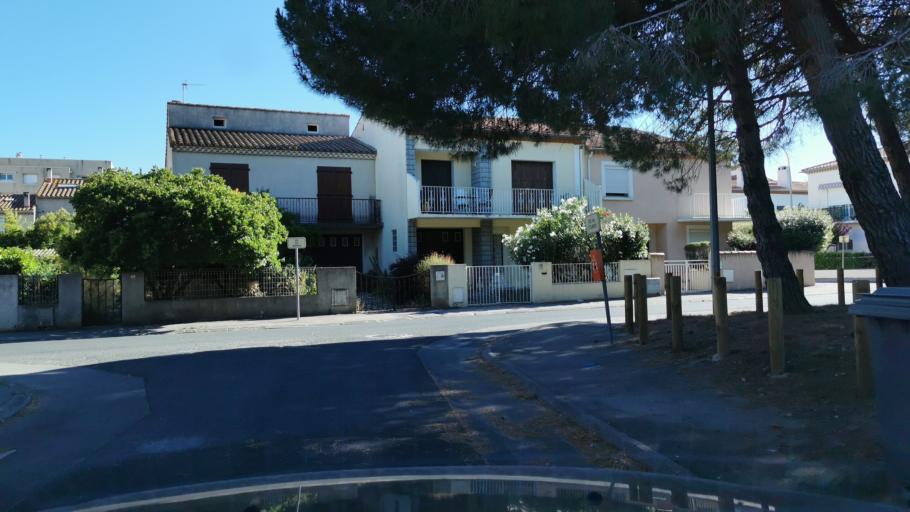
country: FR
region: Languedoc-Roussillon
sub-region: Departement de l'Aude
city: Narbonne
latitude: 43.1876
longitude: 3.0245
